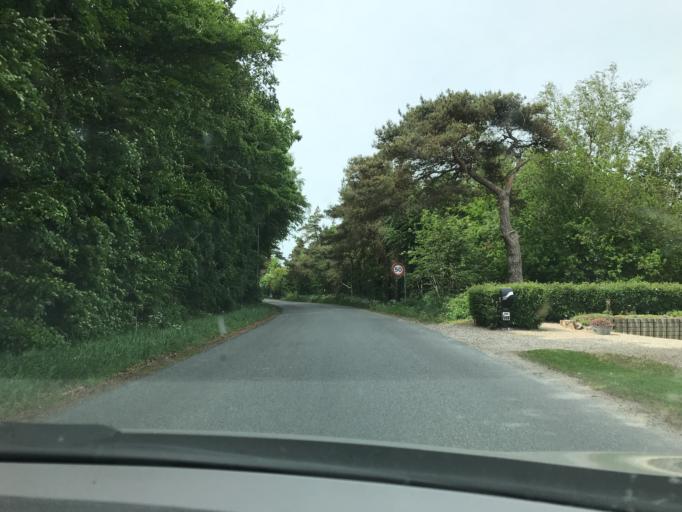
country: DK
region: Central Jutland
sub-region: Norddjurs Kommune
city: Allingabro
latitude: 56.6024
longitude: 10.3081
